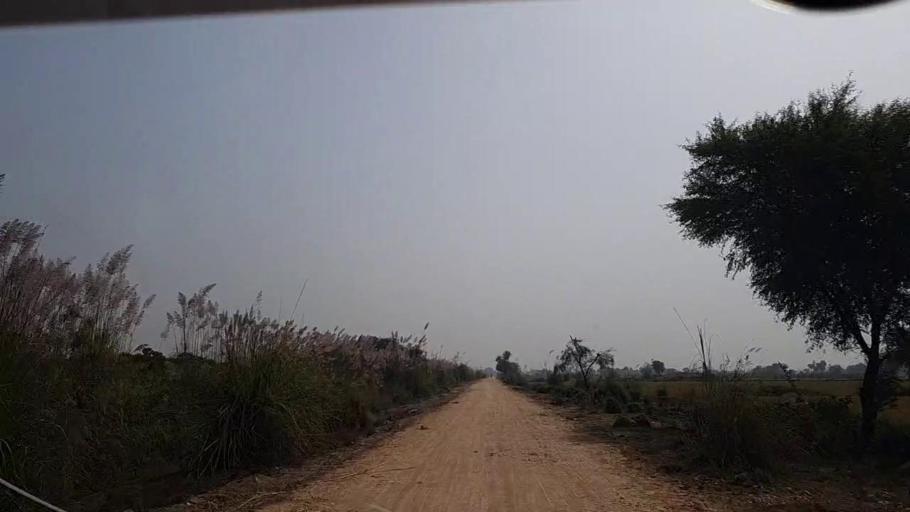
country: PK
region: Sindh
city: Garhi Yasin
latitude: 27.9293
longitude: 68.5599
